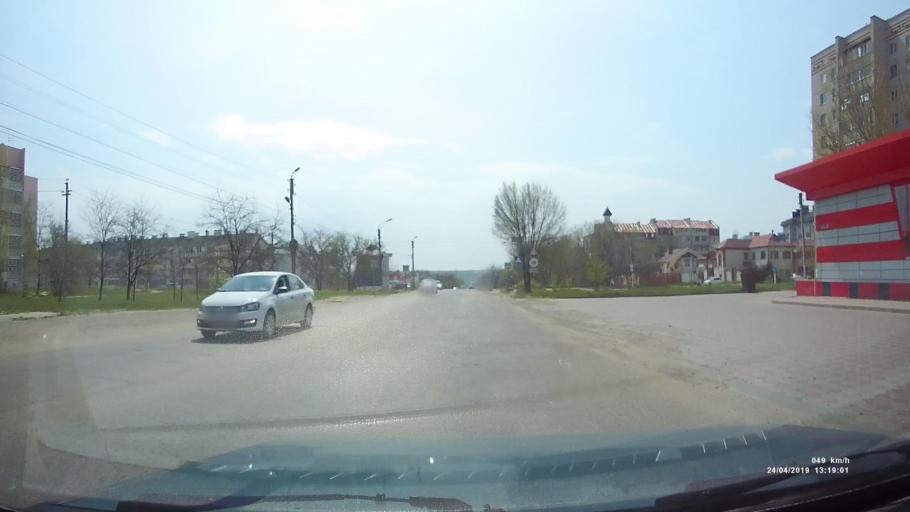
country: RU
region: Kalmykiya
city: Elista
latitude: 46.3019
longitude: 44.2933
